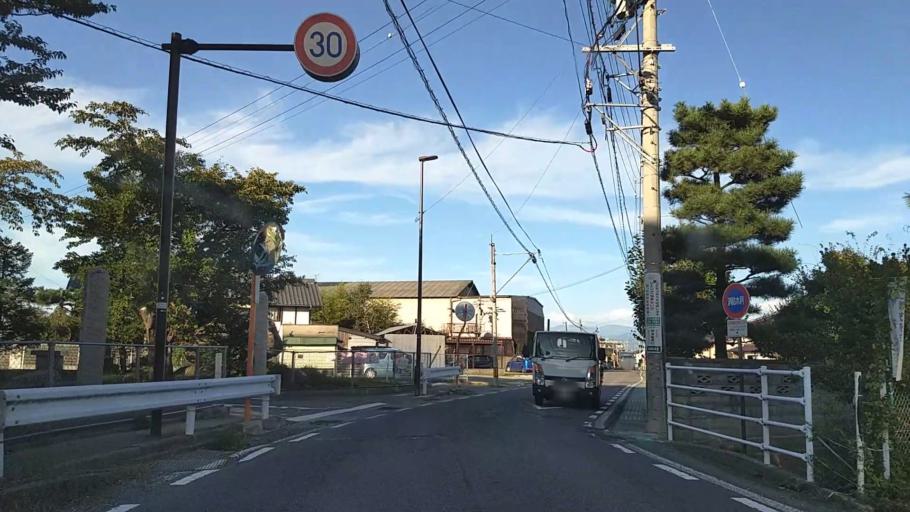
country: JP
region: Nagano
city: Nagano-shi
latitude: 36.6052
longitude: 138.2095
